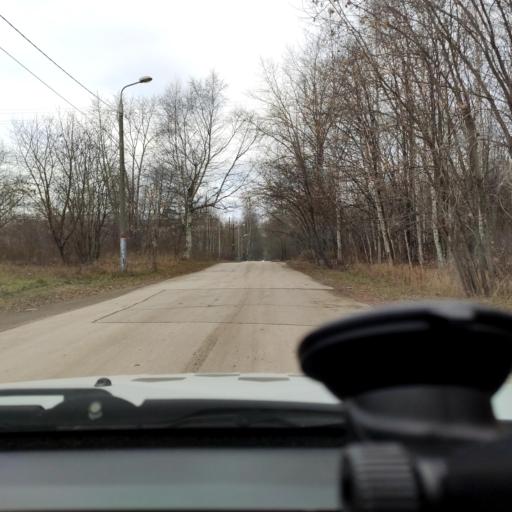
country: RU
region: Perm
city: Perm
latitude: 58.1181
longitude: 56.3756
